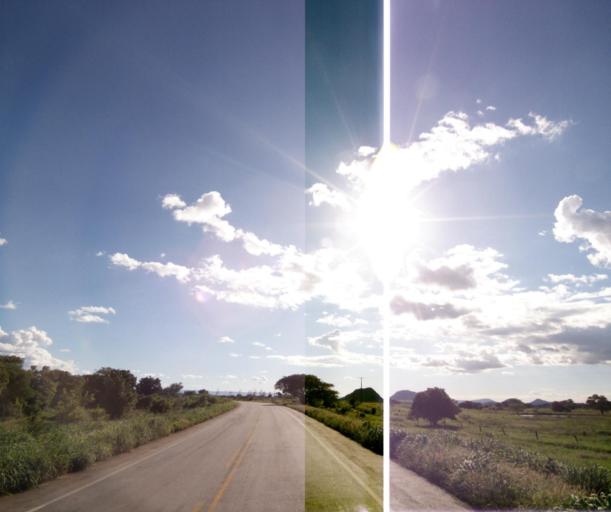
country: BR
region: Bahia
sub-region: Guanambi
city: Guanambi
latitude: -14.1625
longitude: -42.7173
